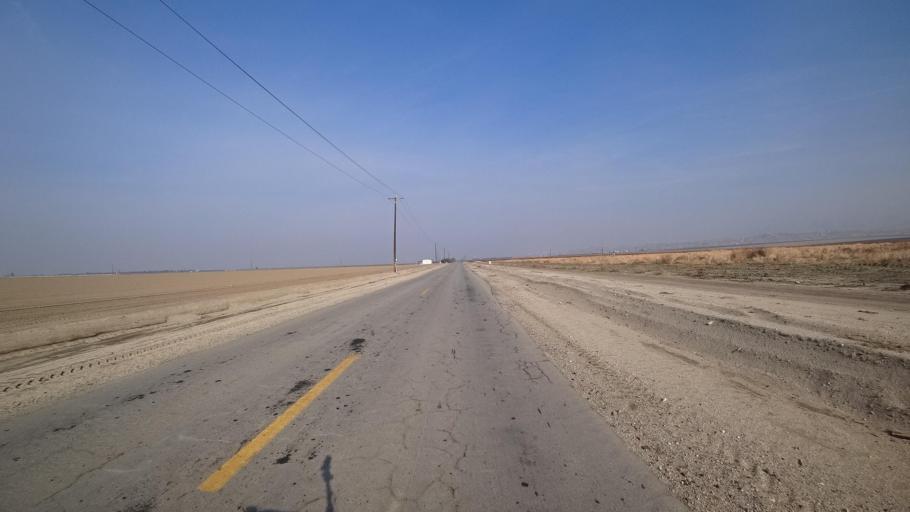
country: US
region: California
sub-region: Kern County
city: Arvin
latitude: 35.0713
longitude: -118.8465
